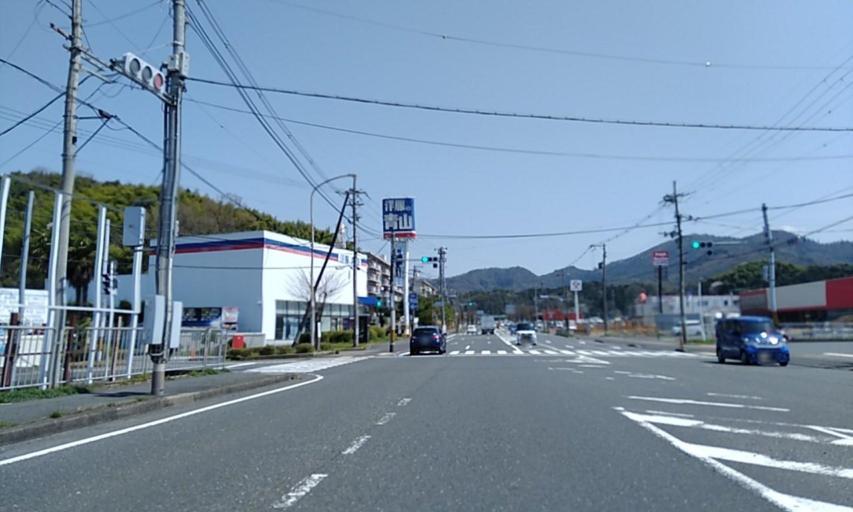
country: JP
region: Kyoto
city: Maizuru
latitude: 35.4511
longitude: 135.3384
